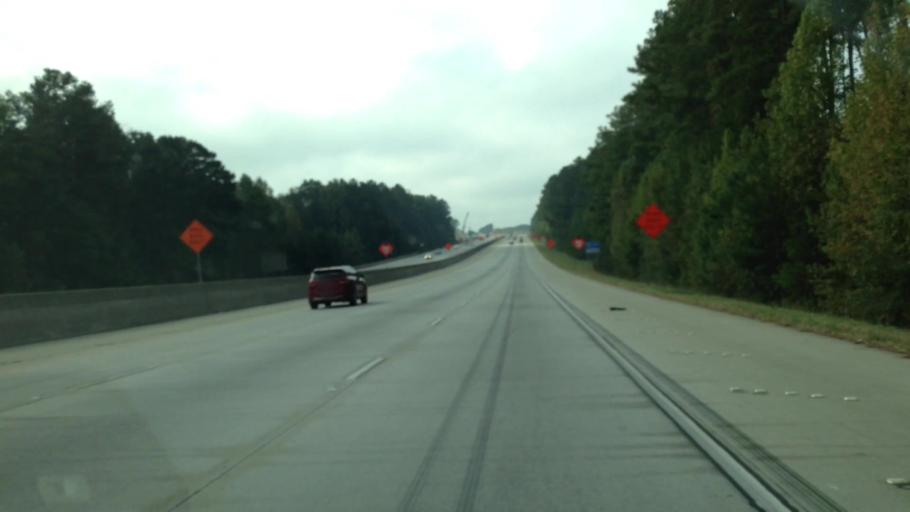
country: US
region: Georgia
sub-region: Coweta County
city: East Newnan
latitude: 33.3744
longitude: -84.7583
